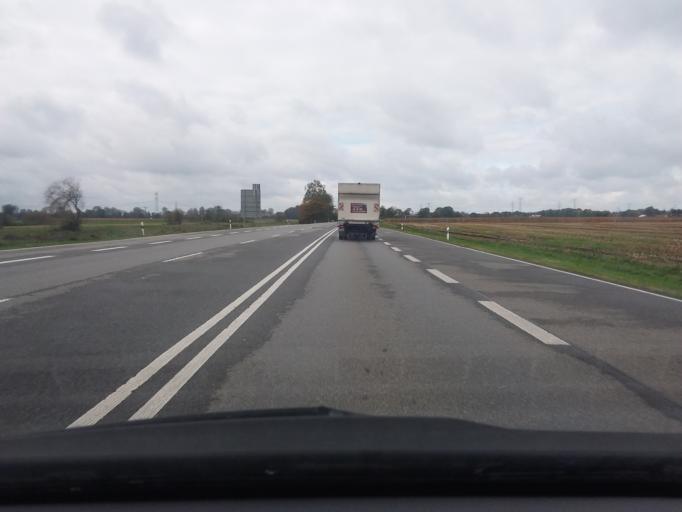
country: DE
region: Bavaria
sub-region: Upper Bavaria
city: Dachau
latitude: 48.2303
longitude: 11.4231
